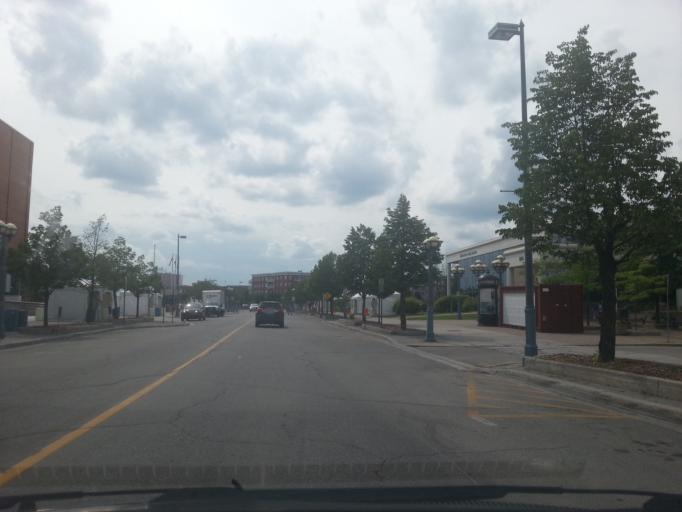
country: CA
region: Quebec
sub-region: Outaouais
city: Gatineau
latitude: 45.4839
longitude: -75.6815
